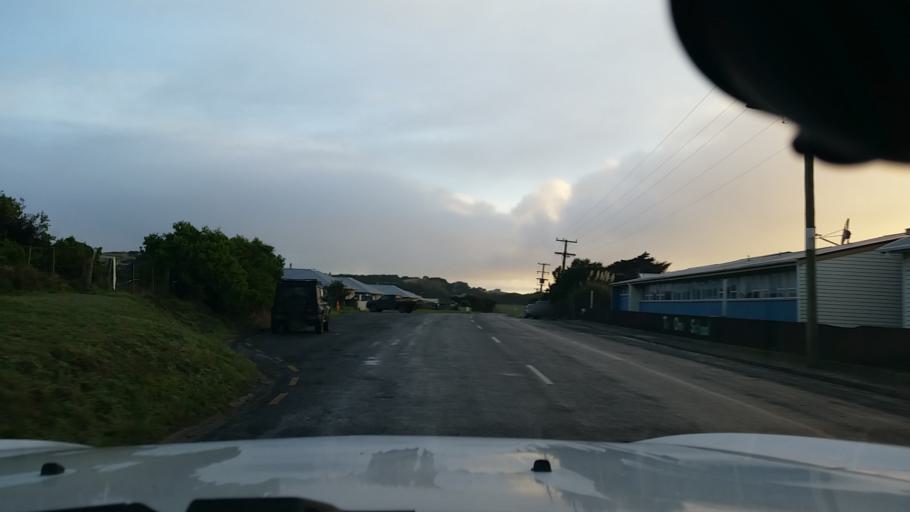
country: NZ
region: Chatham Islands
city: Waitangi
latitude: -43.9336
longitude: -176.5283
